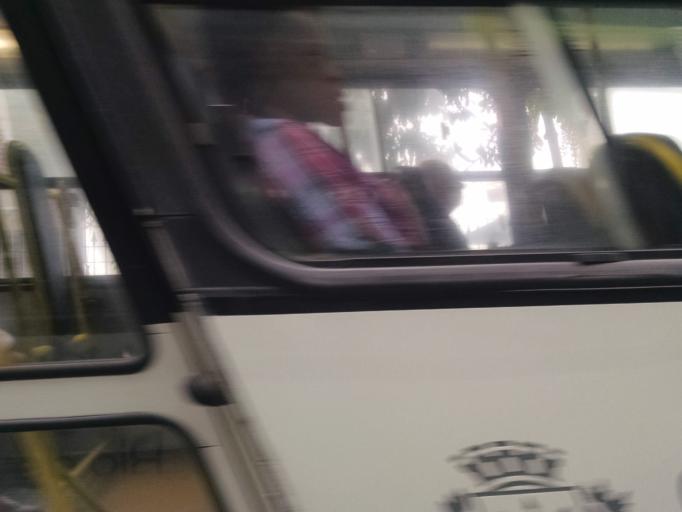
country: BR
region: Rio de Janeiro
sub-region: Rio De Janeiro
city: Rio de Janeiro
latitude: -22.9262
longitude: -43.1912
